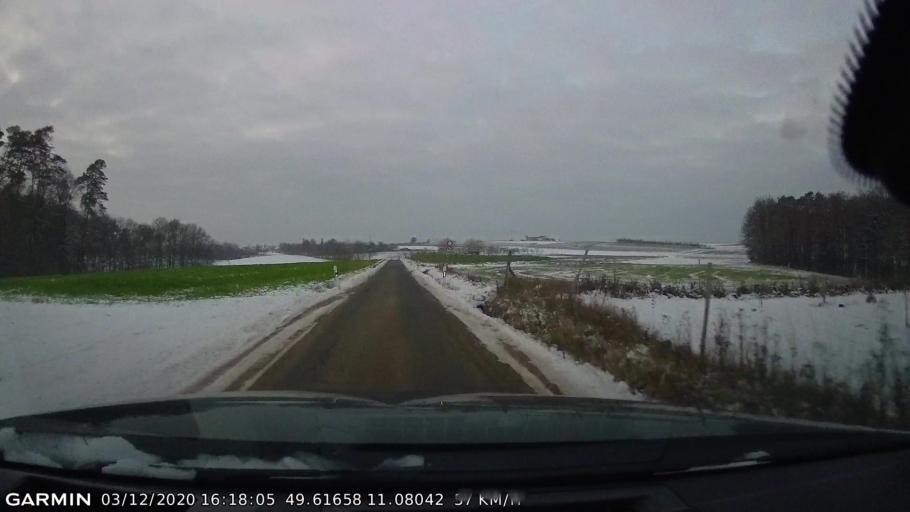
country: DE
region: Bavaria
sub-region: Regierungsbezirk Mittelfranken
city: Marloffstein
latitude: 49.6168
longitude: 11.0800
